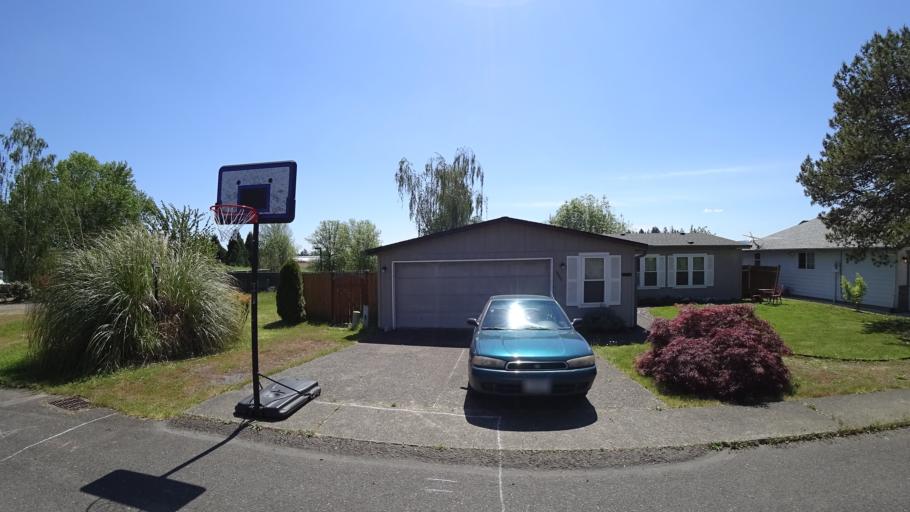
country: US
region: Oregon
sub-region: Washington County
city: Hillsboro
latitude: 45.5049
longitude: -122.9693
